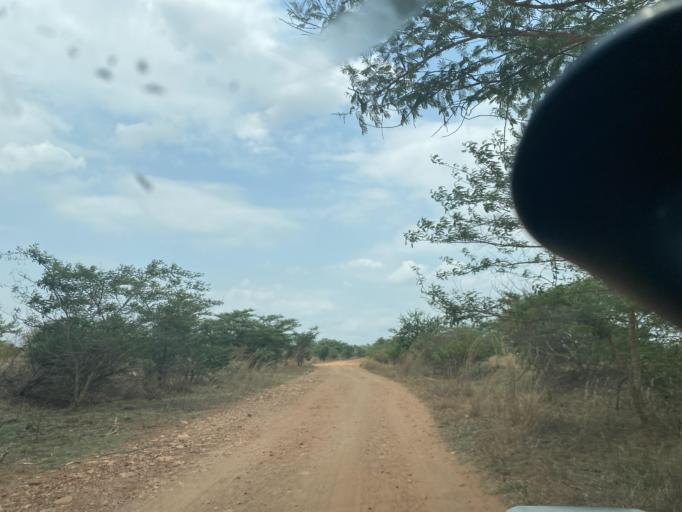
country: ZM
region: Lusaka
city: Chongwe
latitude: -15.5304
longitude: 28.8254
